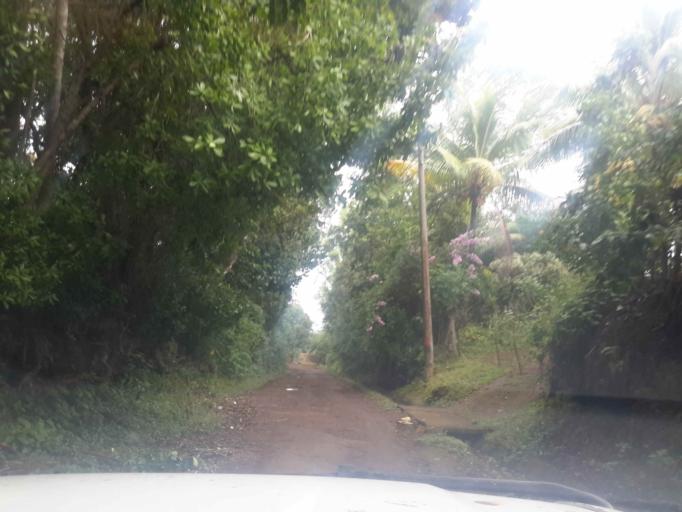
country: NI
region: Carazo
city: San Marcos
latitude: 11.8884
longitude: -86.1802
